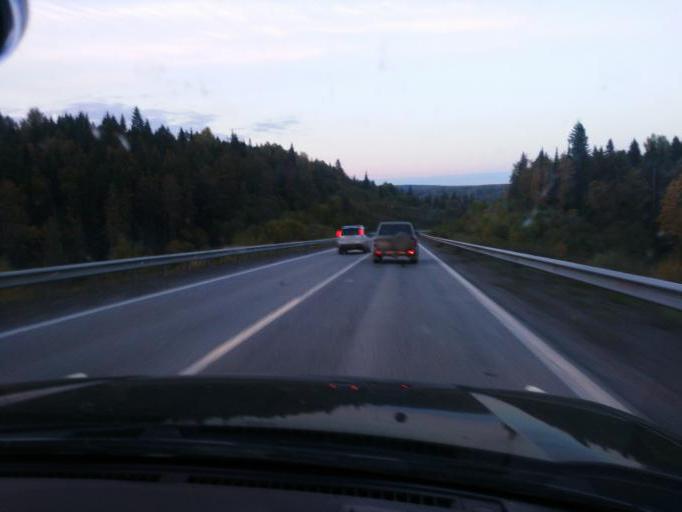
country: RU
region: Perm
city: Sylva
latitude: 58.2954
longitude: 56.7568
